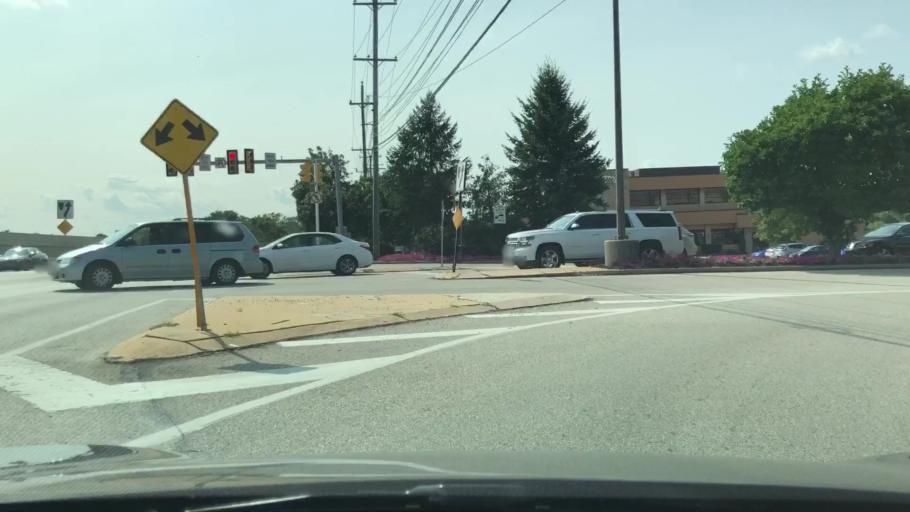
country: US
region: Pennsylvania
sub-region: Montgomery County
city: King of Prussia
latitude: 40.0855
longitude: -75.3932
